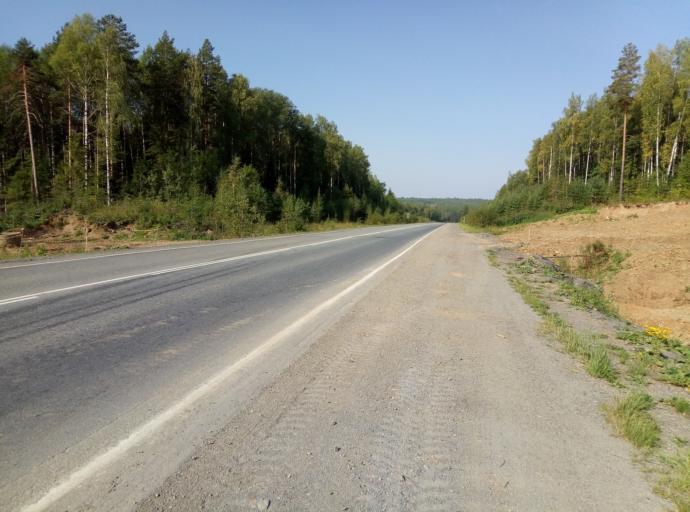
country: RU
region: Sverdlovsk
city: Krasnotur'insk
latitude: 59.6689
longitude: 60.1814
